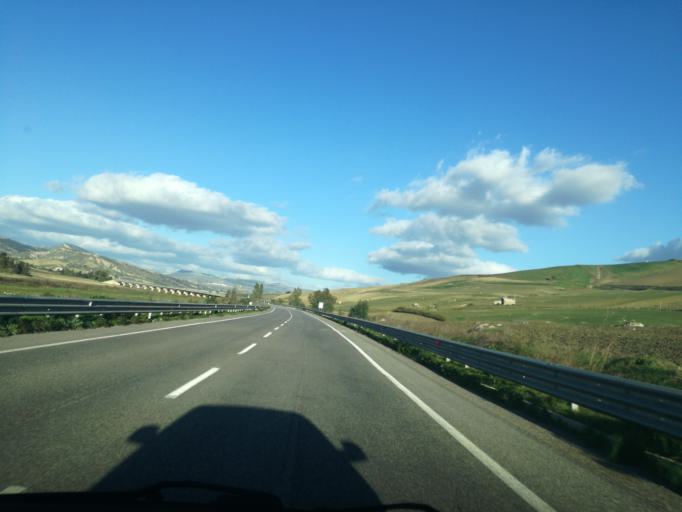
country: IT
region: Sicily
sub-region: Enna
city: Pietraperzia
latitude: 37.4360
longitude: 14.0924
